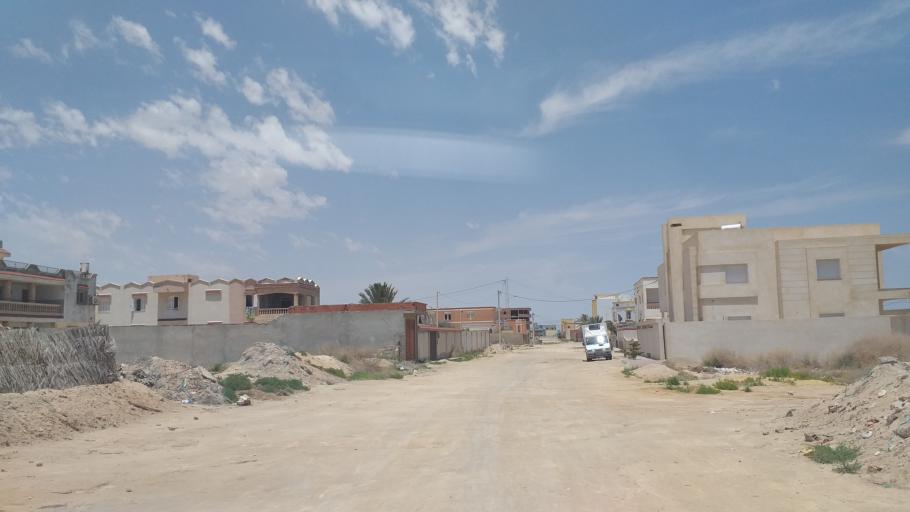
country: TN
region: Qabis
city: Gabes
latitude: 33.9502
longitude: 10.0723
